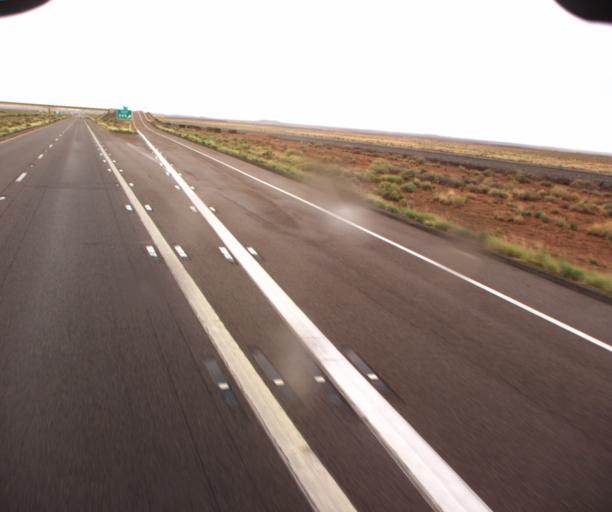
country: US
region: Arizona
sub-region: Coconino County
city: LeChee
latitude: 35.0685
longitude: -110.8395
